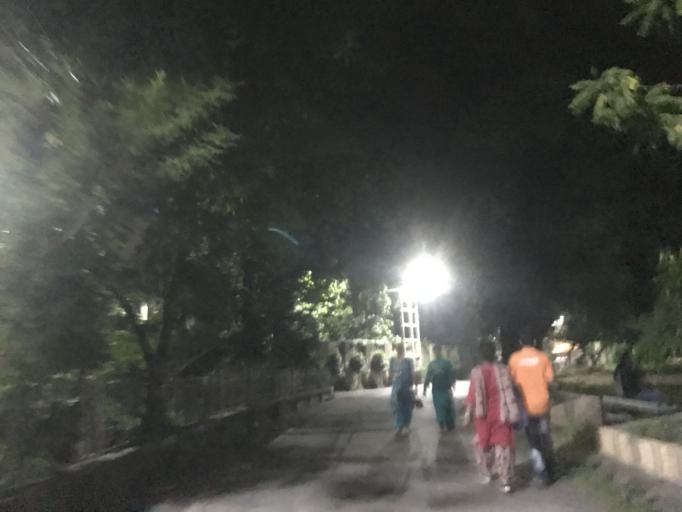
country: IN
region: West Bengal
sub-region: Kolkata
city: Kolkata
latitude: 22.6004
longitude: 88.3764
